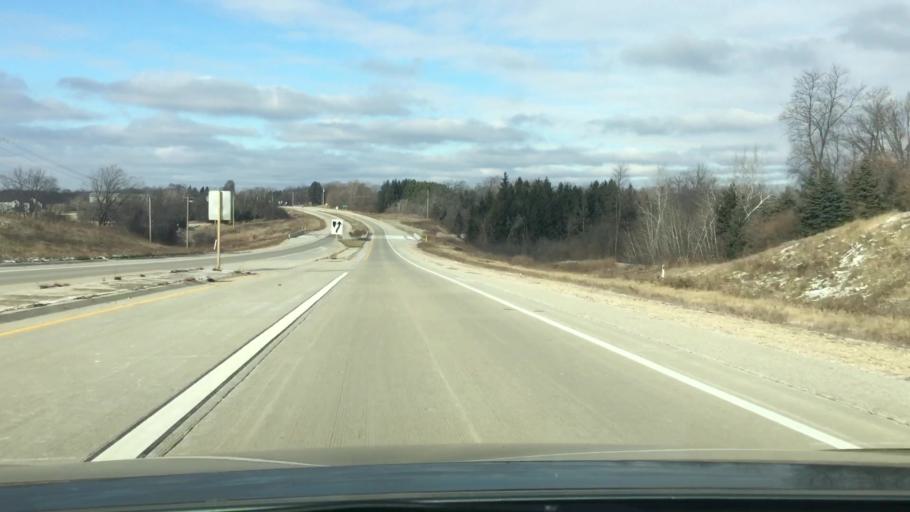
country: US
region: Wisconsin
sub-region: Waukesha County
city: North Prairie
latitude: 42.9416
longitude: -88.3476
